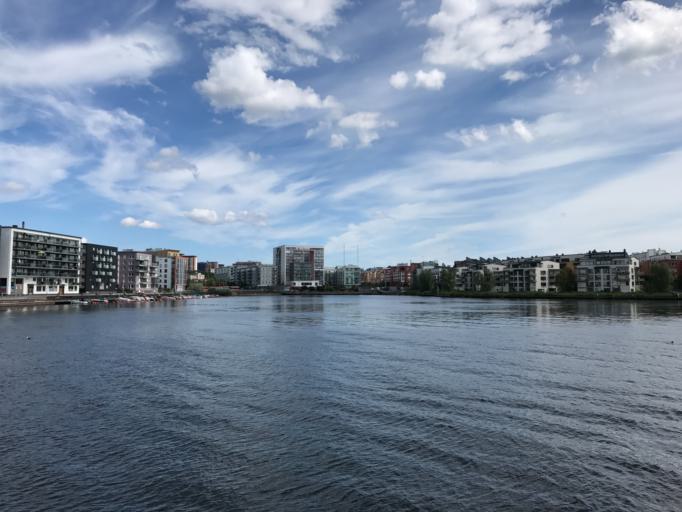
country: SE
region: Stockholm
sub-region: Stockholms Kommun
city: OEstermalm
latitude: 59.3078
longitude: 18.0995
